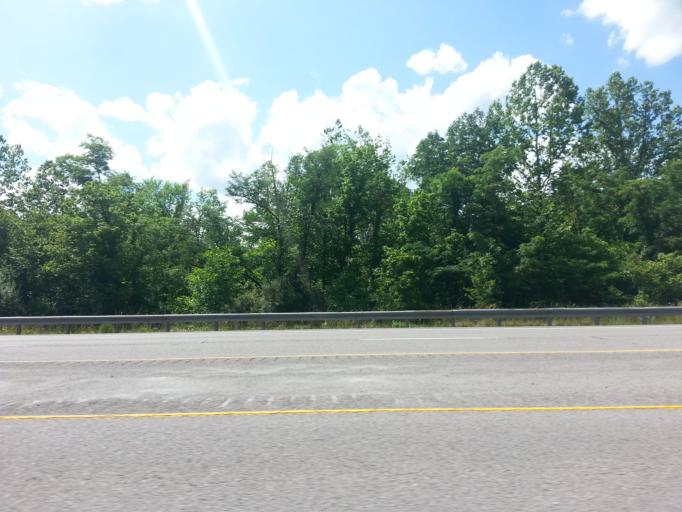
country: US
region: Kentucky
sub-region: Harlan County
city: Harlan
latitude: 36.8640
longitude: -83.3179
